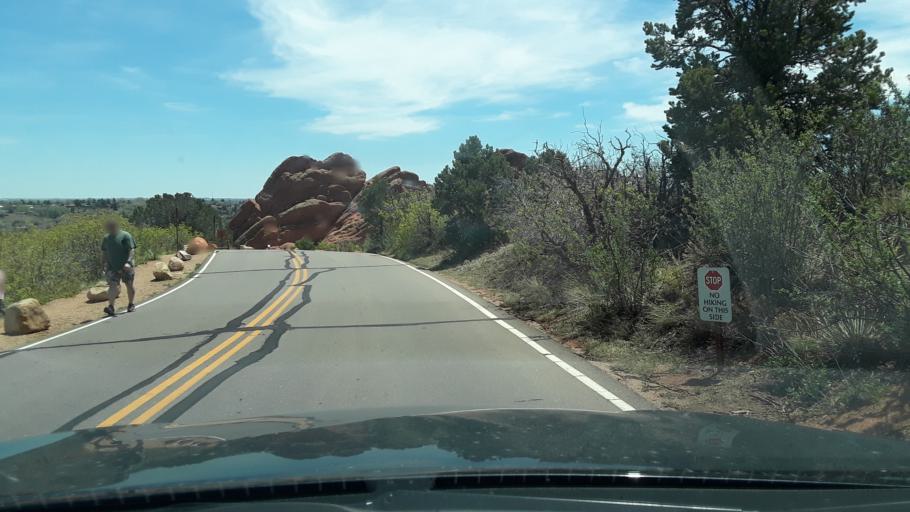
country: US
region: Colorado
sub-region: El Paso County
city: Manitou Springs
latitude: 38.8655
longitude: -104.8785
